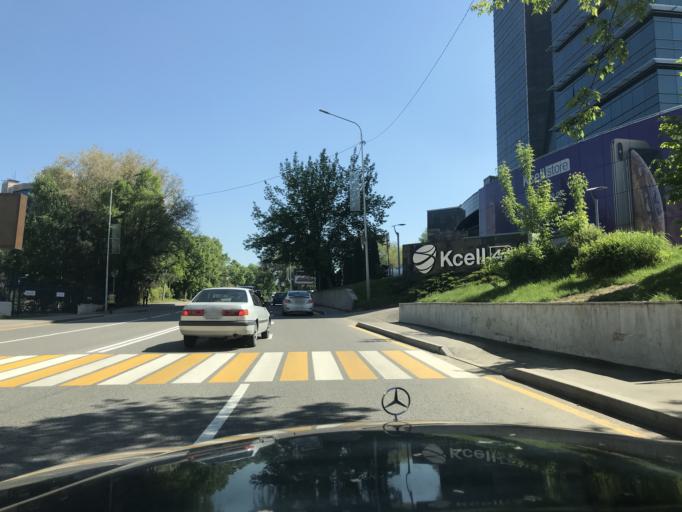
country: KZ
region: Almaty Qalasy
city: Almaty
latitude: 43.2338
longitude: 76.9394
